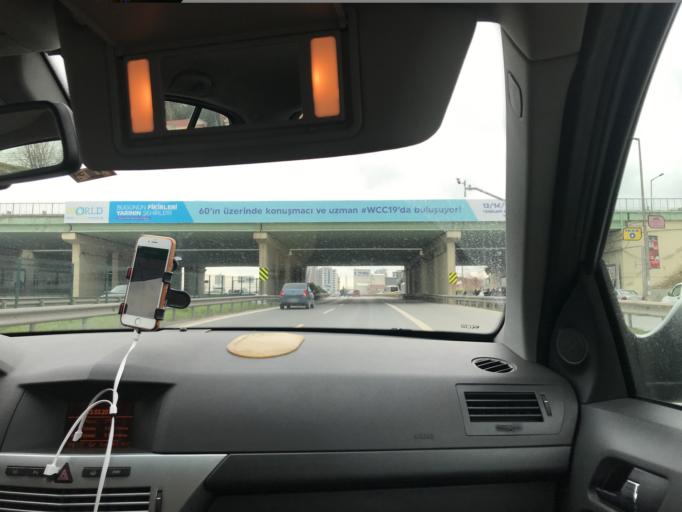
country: TR
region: Istanbul
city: Maltepe
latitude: 40.9059
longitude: 29.2119
